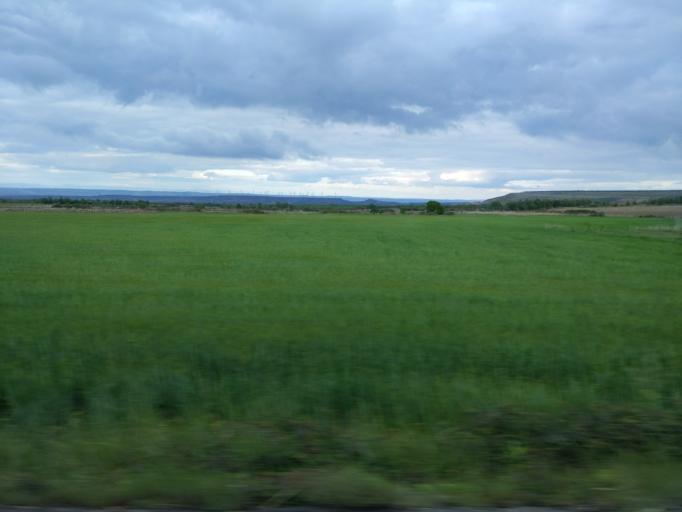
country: ES
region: La Rioja
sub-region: Provincia de La Rioja
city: Tudelilla
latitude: 42.2873
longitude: -2.0965
